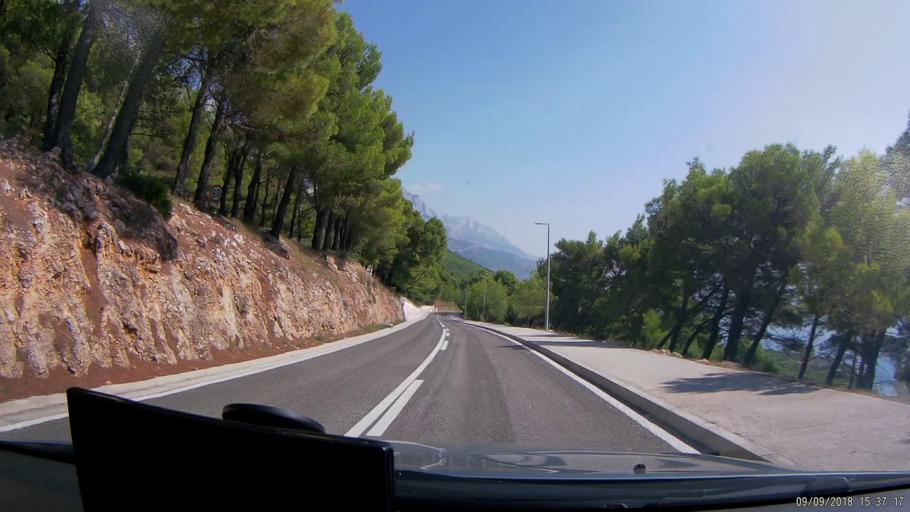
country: HR
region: Splitsko-Dalmatinska
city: Donja Brela
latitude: 43.3737
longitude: 16.9270
